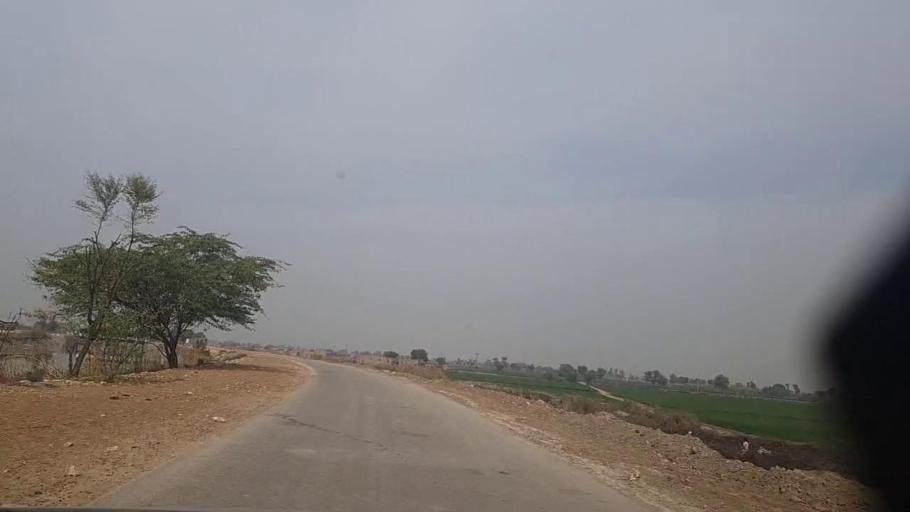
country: PK
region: Sindh
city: Sakrand
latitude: 26.2820
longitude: 68.2270
